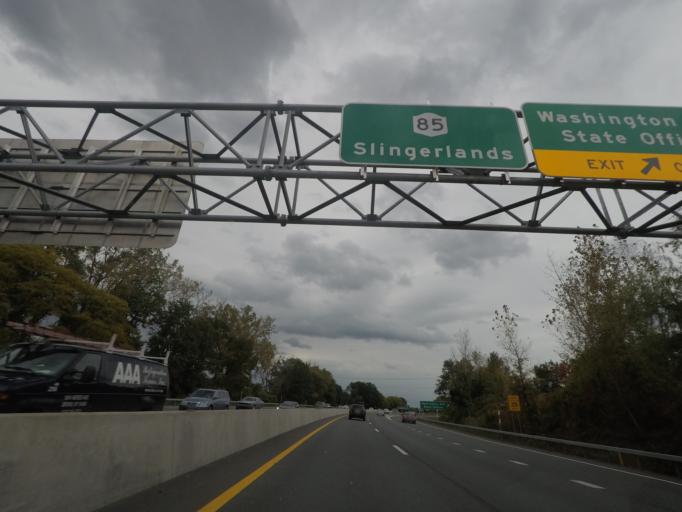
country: US
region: New York
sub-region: Albany County
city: Roessleville
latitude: 42.6837
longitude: -73.8020
